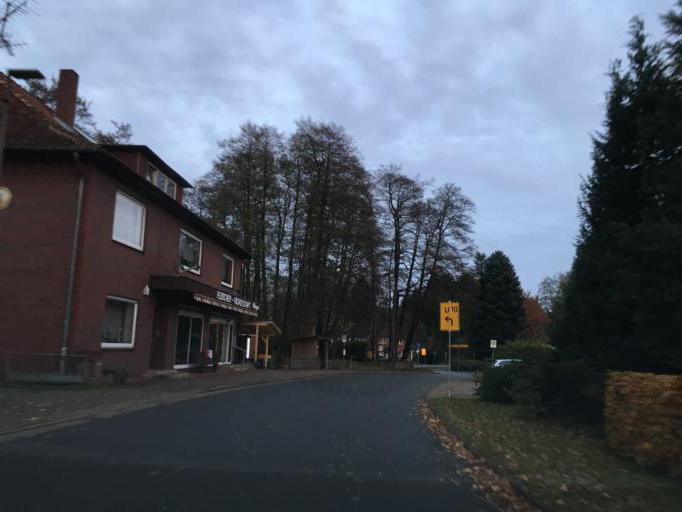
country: DE
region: Lower Saxony
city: Bispingen
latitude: 53.0965
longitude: 10.0255
